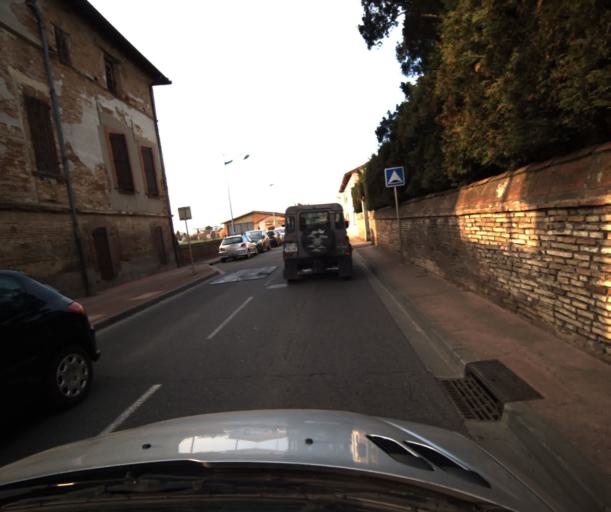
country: FR
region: Midi-Pyrenees
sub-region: Departement de la Haute-Garonne
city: Launaguet
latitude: 43.6747
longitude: 1.4566
